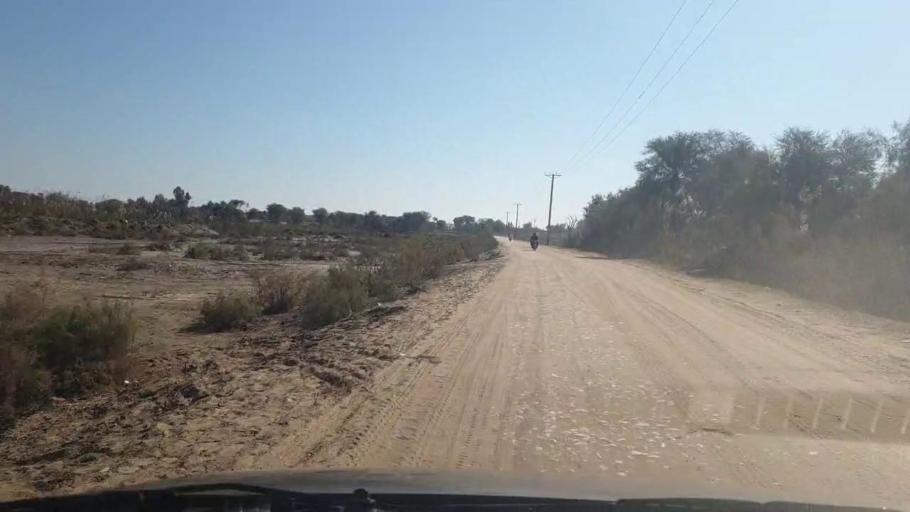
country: PK
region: Sindh
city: Bozdar
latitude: 27.0741
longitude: 68.6162
